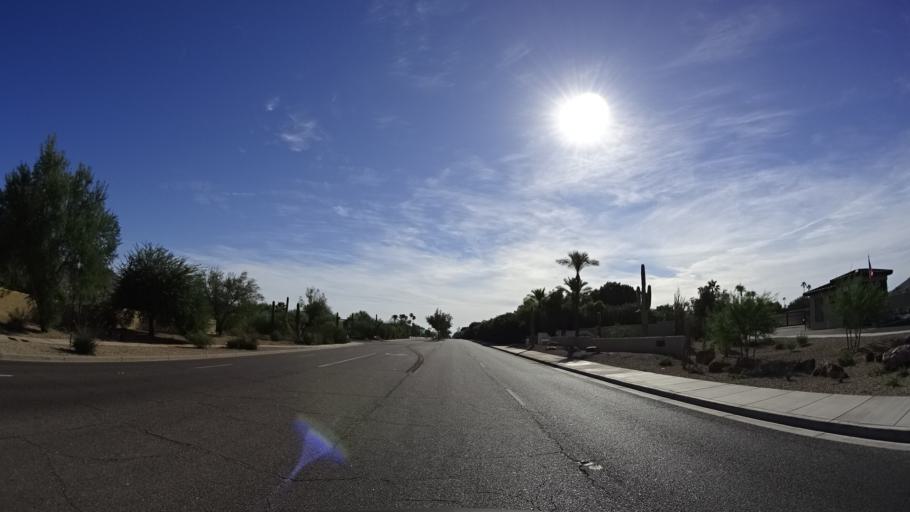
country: US
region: Arizona
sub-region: Maricopa County
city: Paradise Valley
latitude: 33.5310
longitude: -111.9590
